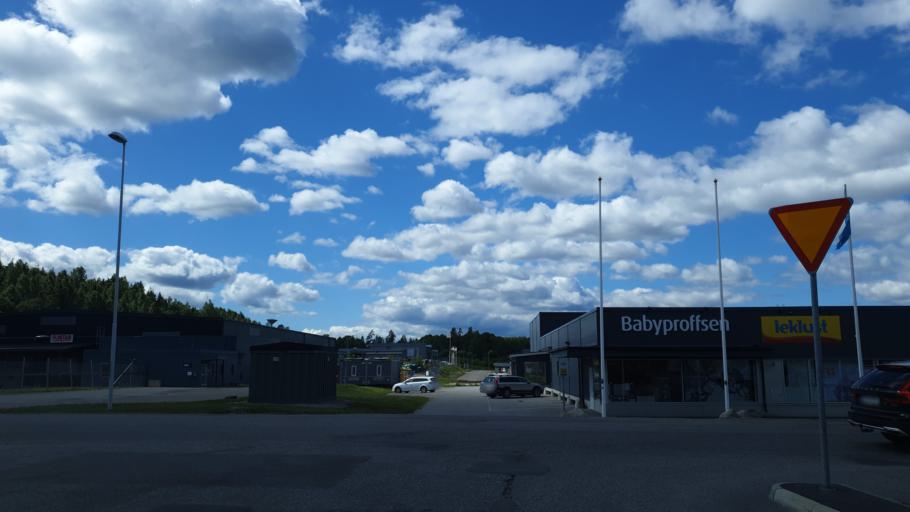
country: SE
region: Vaesternorrland
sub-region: Sundsvalls Kommun
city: Sundsbruk
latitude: 62.4402
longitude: 17.3312
